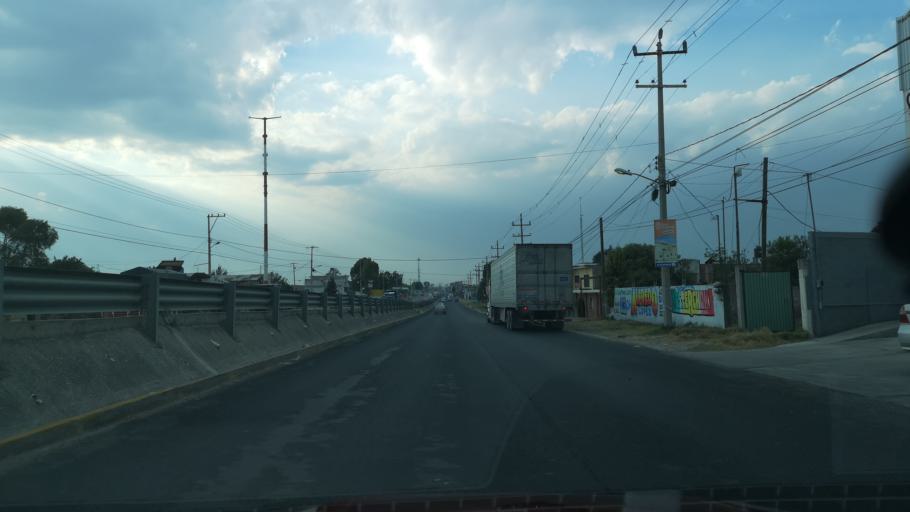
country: MX
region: Puebla
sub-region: Juan C. Bonilla
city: Santa Maria Zacatepec
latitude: 19.1138
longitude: -98.3571
